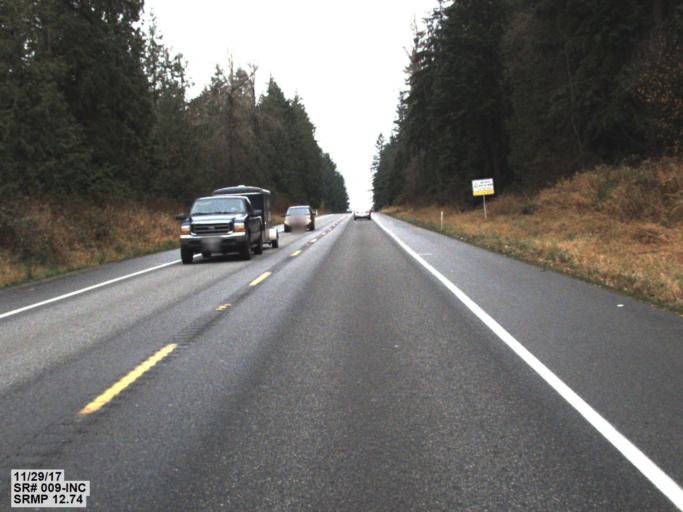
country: US
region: Washington
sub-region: Snohomish County
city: Fobes Hill
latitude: 47.9593
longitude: -122.1018
